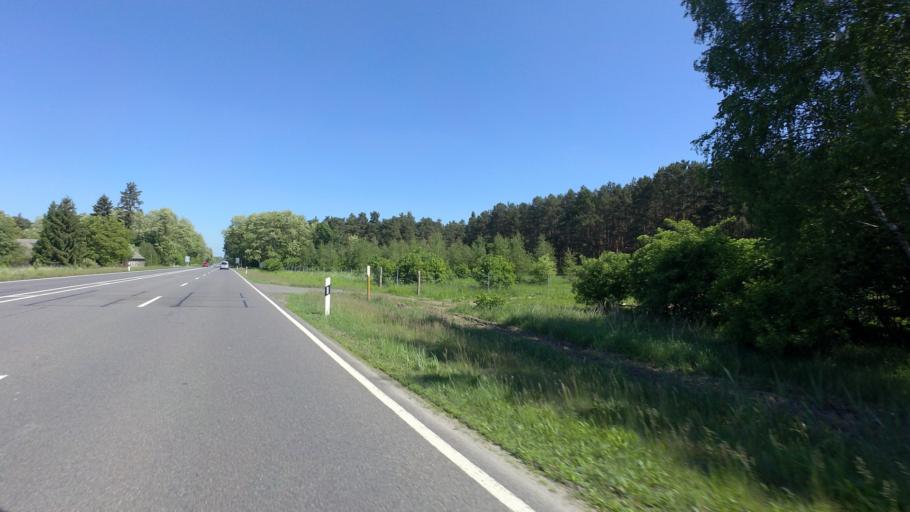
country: DE
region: Brandenburg
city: Spremberg
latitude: 51.6181
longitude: 14.3630
